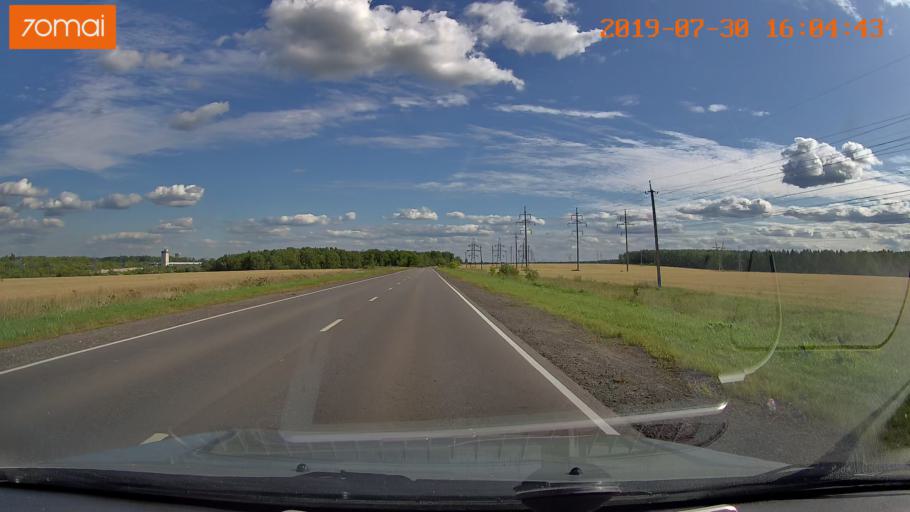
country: RU
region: Moskovskaya
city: Lopatinskiy
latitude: 55.2771
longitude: 38.7100
